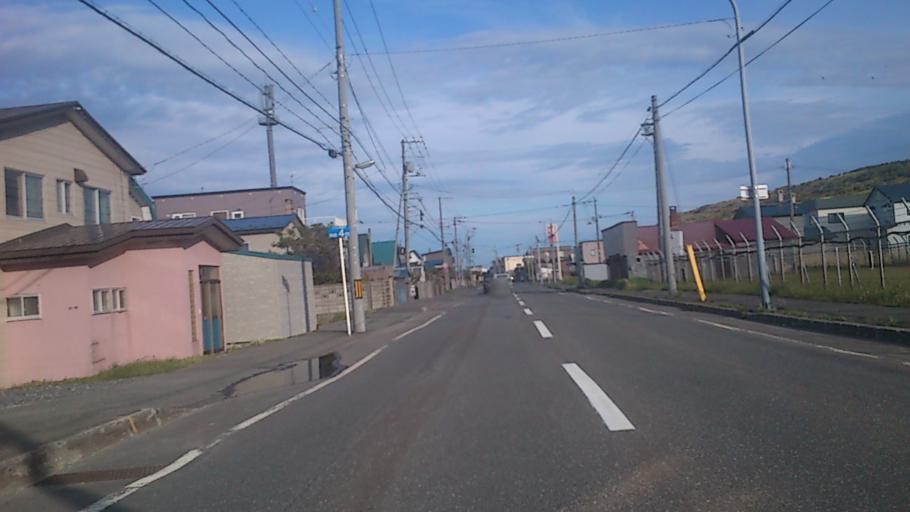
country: JP
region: Hokkaido
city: Wakkanai
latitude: 45.4418
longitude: 141.6540
